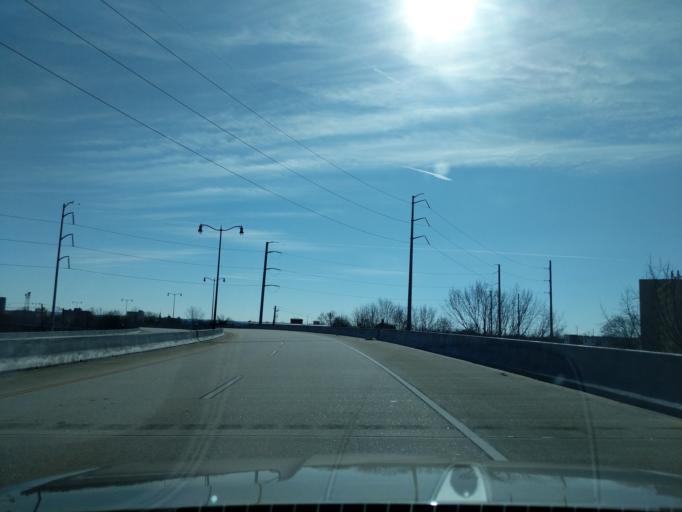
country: US
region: Georgia
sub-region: Richmond County
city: Augusta
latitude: 33.4768
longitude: -81.9837
